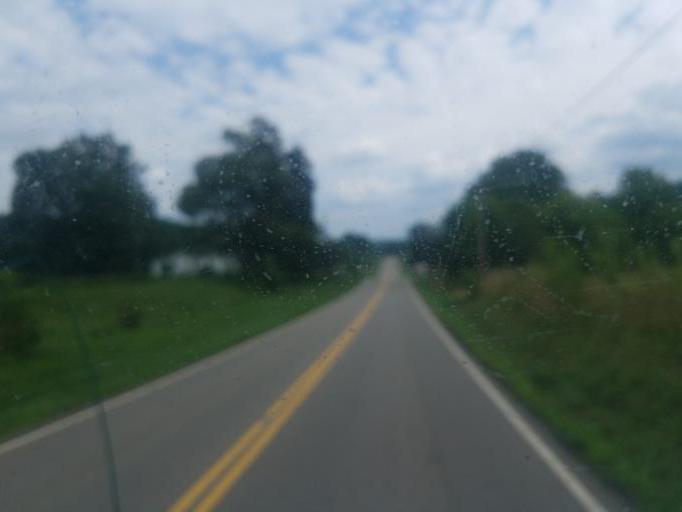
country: US
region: Ohio
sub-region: Licking County
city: Utica
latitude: 40.1638
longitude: -82.4833
